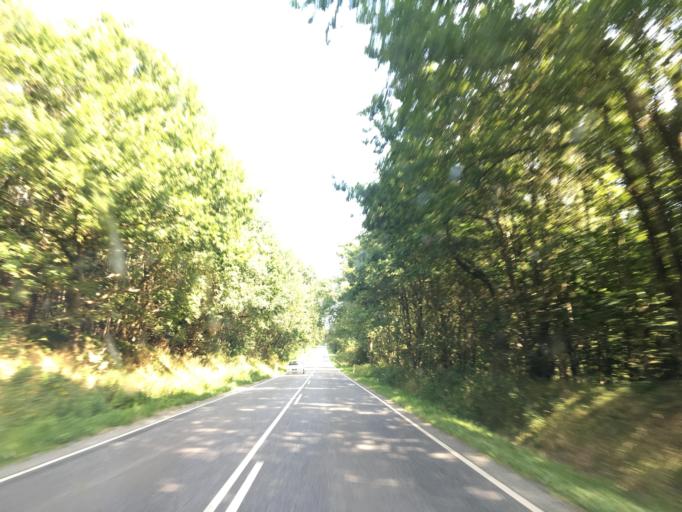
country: DK
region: South Denmark
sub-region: Middelfart Kommune
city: Ejby
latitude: 55.3897
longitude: 9.9259
